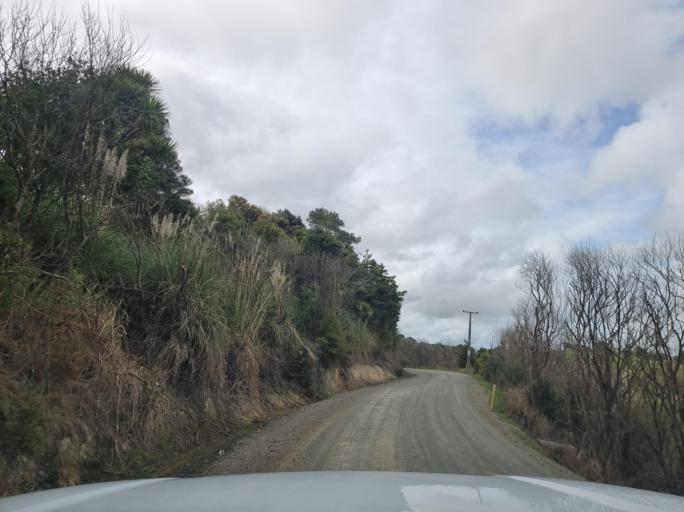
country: NZ
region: Northland
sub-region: Whangarei
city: Ruakaka
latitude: -36.1112
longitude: 174.2119
